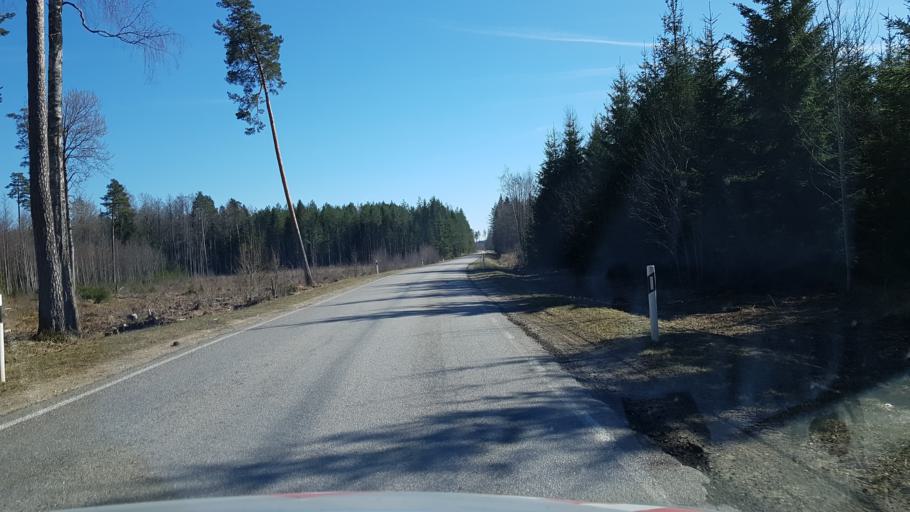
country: EE
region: Laeaene-Virumaa
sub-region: Vinni vald
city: Vinni
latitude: 59.2549
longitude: 26.6871
